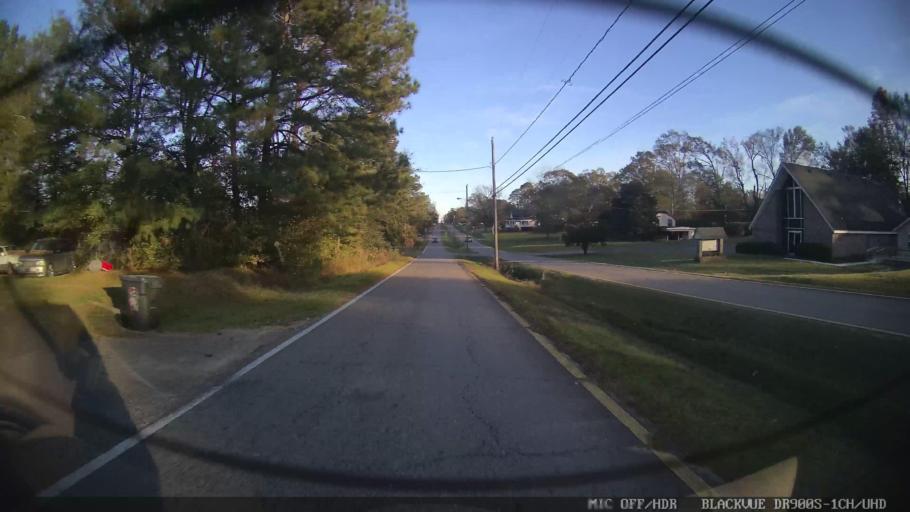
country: US
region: Mississippi
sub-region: Lamar County
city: Lumberton
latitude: 31.0056
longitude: -89.4635
